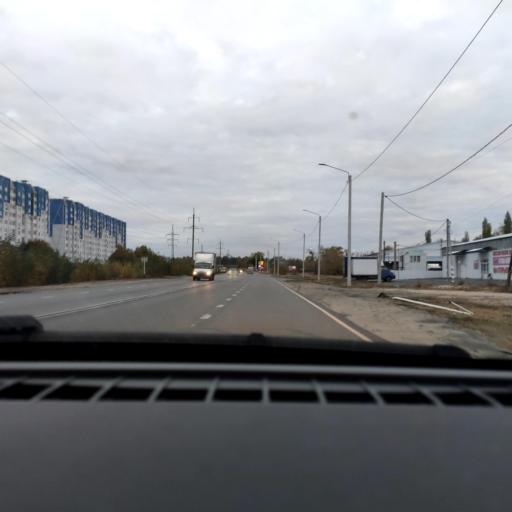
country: RU
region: Voronezj
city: Maslovka
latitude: 51.5917
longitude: 39.2485
